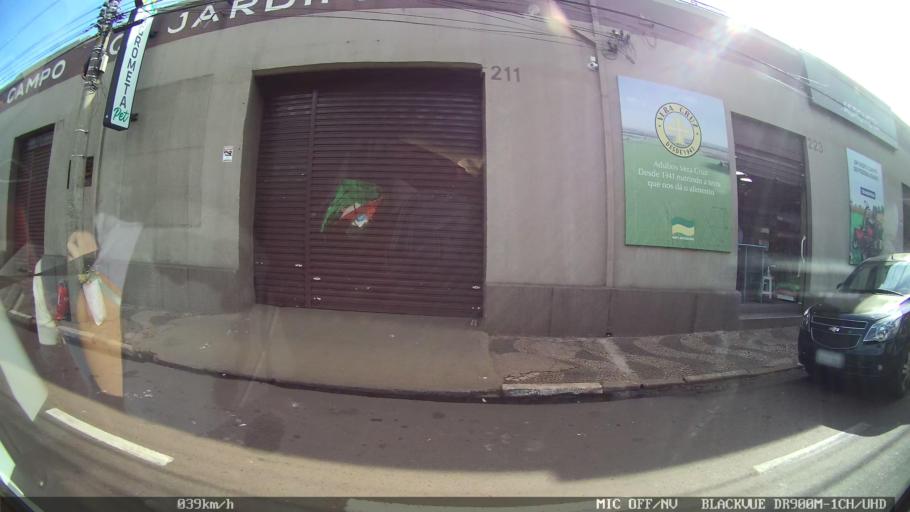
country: BR
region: Sao Paulo
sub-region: Araraquara
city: Araraquara
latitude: -21.7971
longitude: -48.1712
